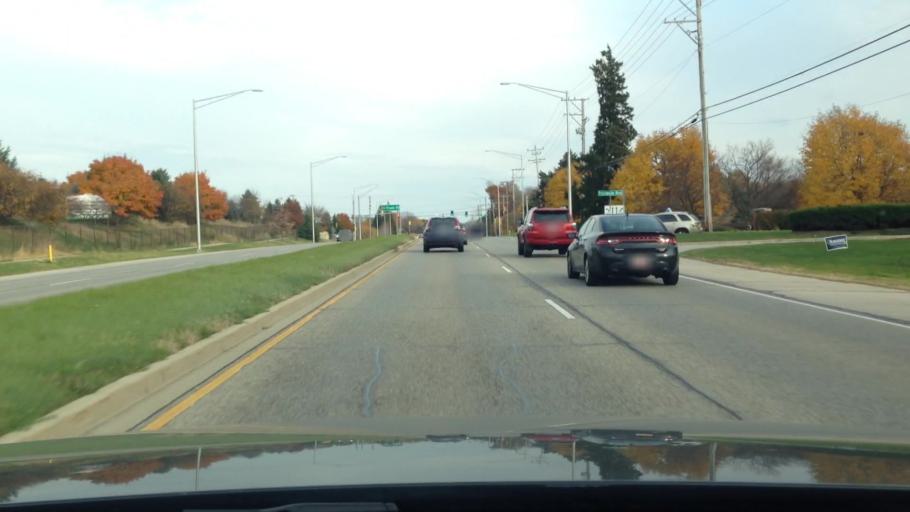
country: US
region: Illinois
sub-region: McHenry County
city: Lake in the Hills
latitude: 42.1757
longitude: -88.3669
